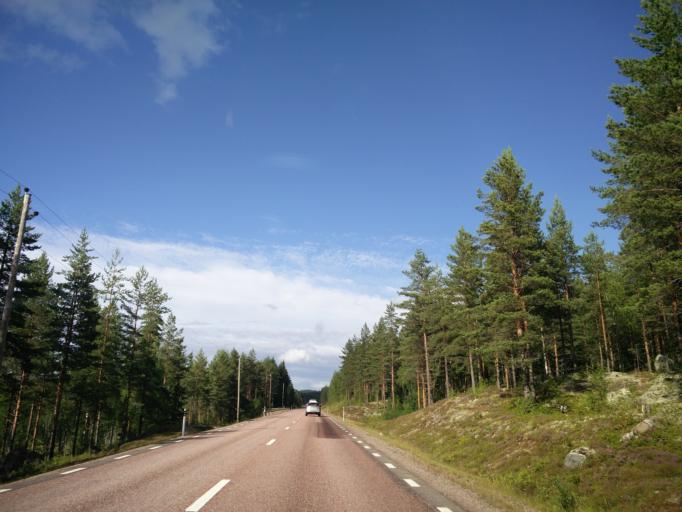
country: SE
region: Vaermland
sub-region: Hagfors Kommun
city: Ekshaerad
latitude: 60.4427
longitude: 13.2718
